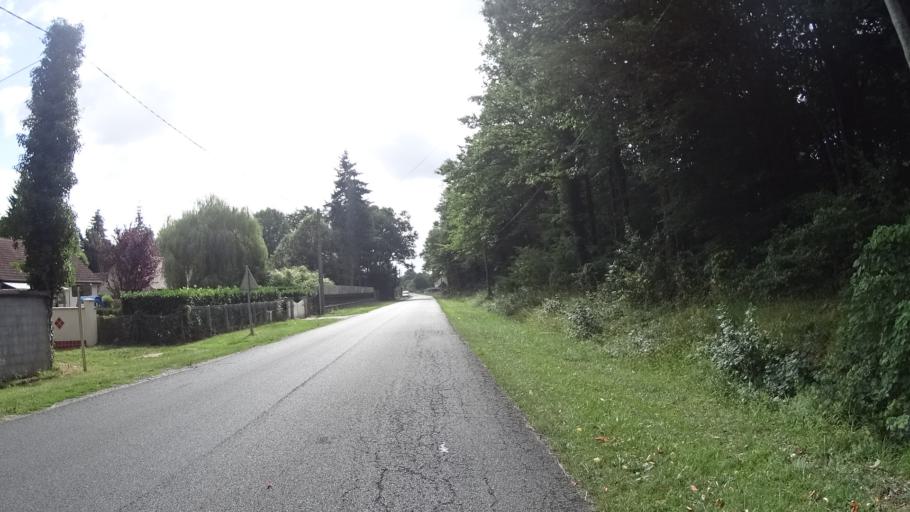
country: FR
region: Centre
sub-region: Departement du Loiret
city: Lorris
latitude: 47.8920
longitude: 2.4902
